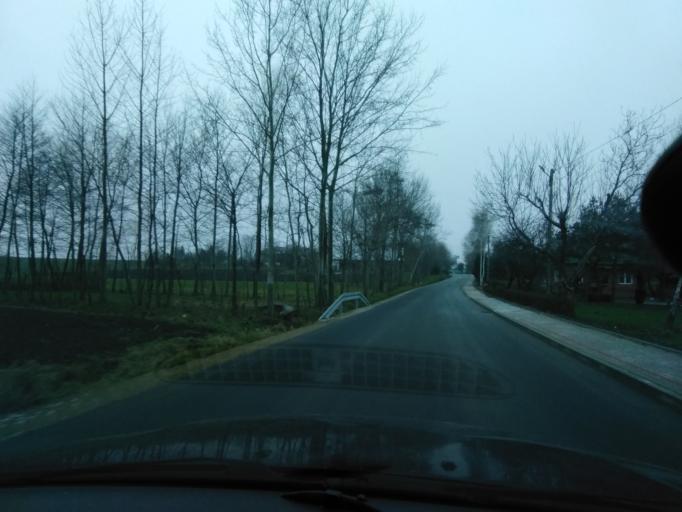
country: PL
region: Subcarpathian Voivodeship
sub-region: Powiat przeworski
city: Kanczuga
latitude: 50.0148
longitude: 22.4160
